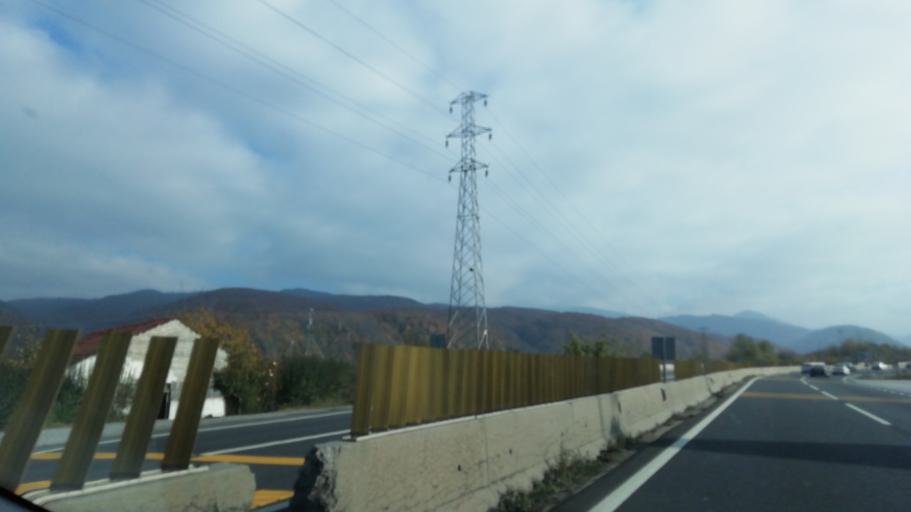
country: TR
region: Duzce
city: Kaynasli
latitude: 40.7712
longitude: 31.3523
